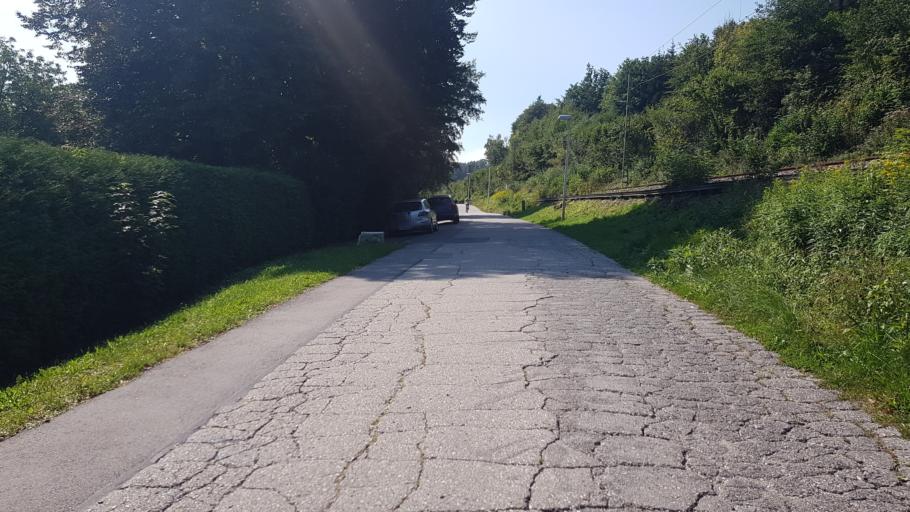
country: DE
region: Bavaria
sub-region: Upper Bavaria
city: Herrsching am Ammersee
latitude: 48.0241
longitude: 11.1779
